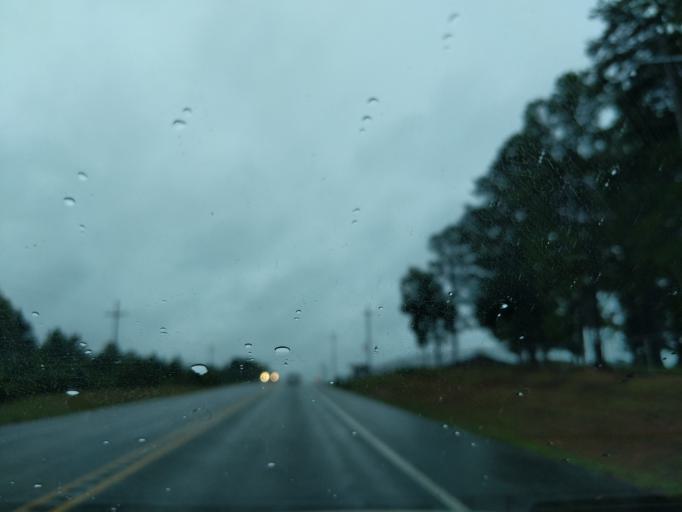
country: US
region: Louisiana
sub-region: Webster Parish
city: Minden
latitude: 32.6064
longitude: -93.2498
